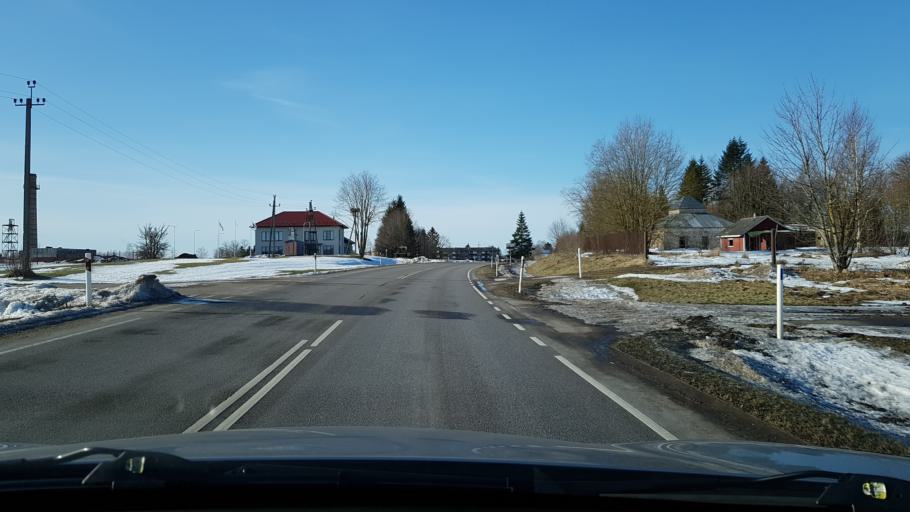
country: EE
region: Viljandimaa
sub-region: Vohma linn
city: Vohma
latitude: 58.6324
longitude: 25.7340
